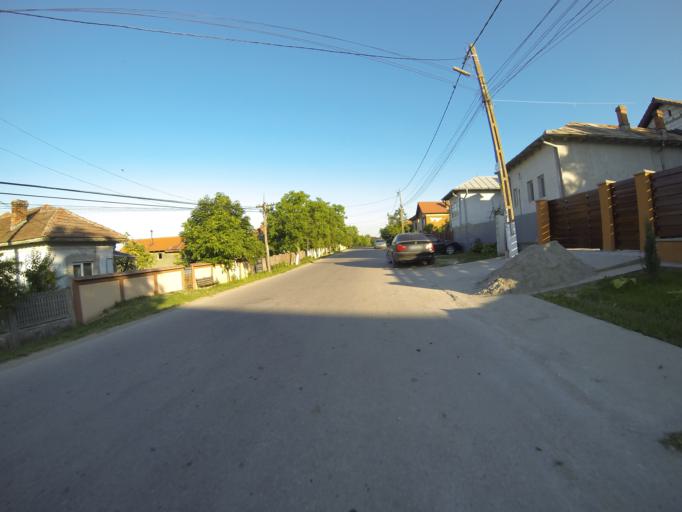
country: RO
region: Dolj
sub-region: Comuna Tuglui
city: Tuglui
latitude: 44.1990
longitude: 23.8013
